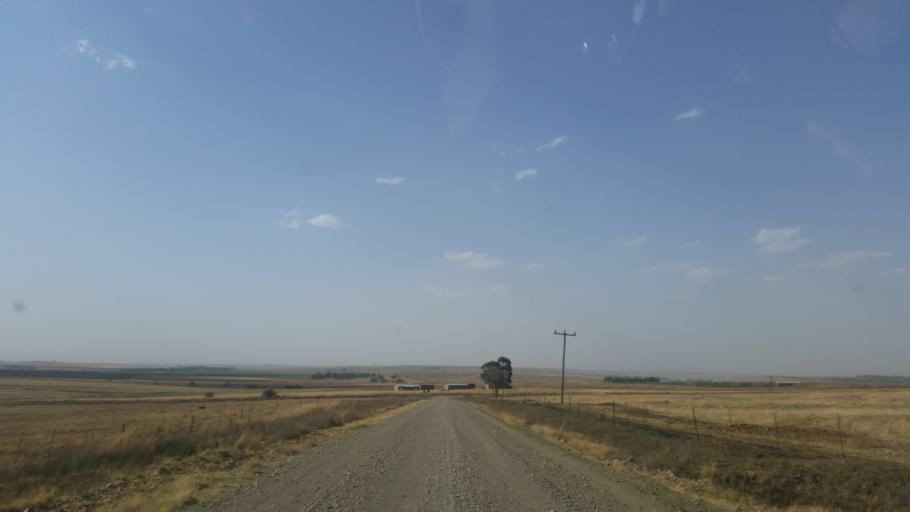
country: ZA
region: Orange Free State
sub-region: Thabo Mofutsanyana District Municipality
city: Phuthaditjhaba
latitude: -28.2112
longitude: 28.6810
